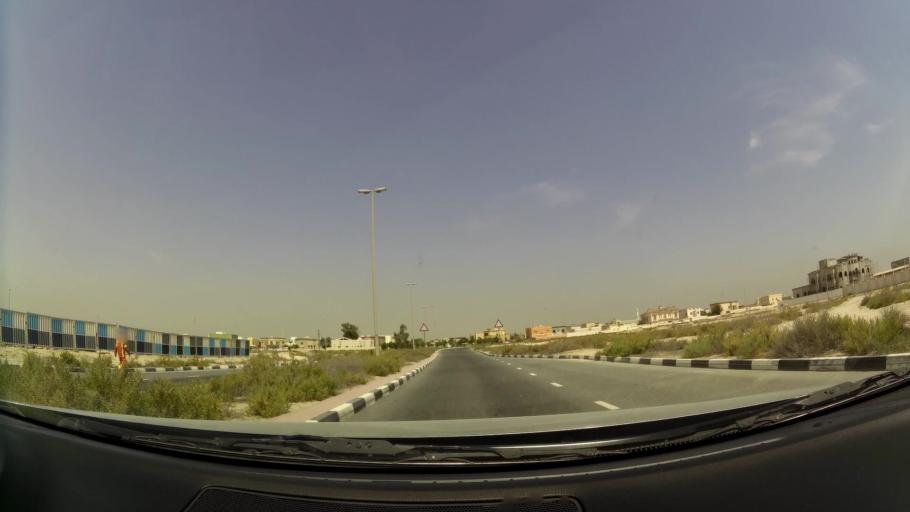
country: AE
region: Ash Shariqah
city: Sharjah
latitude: 25.1840
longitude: 55.4293
